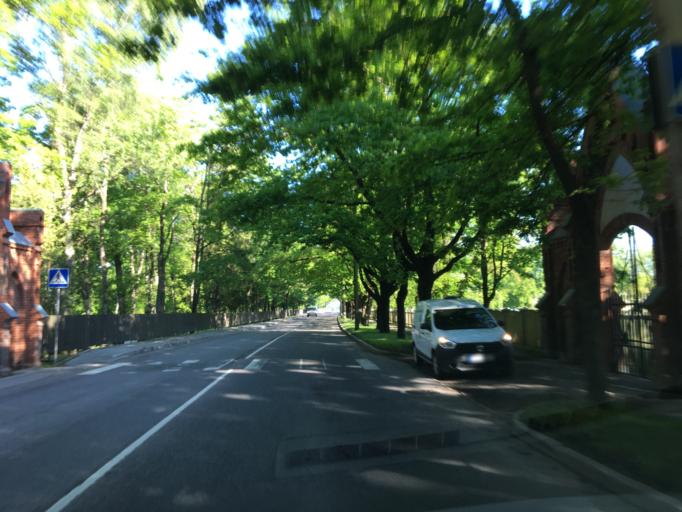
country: EE
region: Tartu
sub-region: Tartu linn
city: Tartu
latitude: 58.3968
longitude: 26.7114
